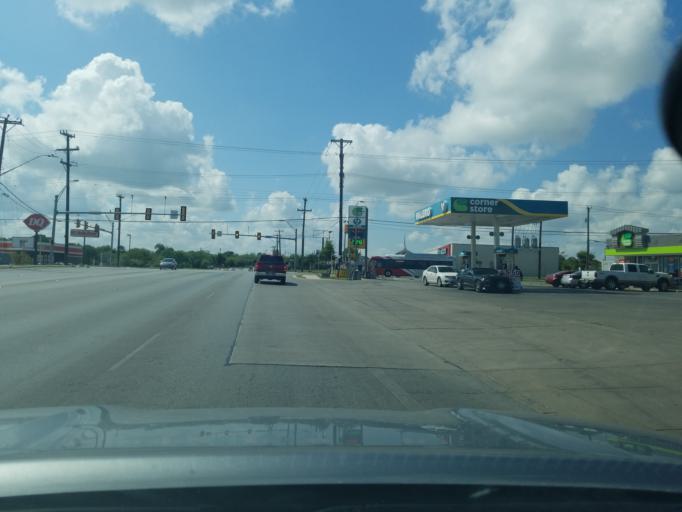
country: US
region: Texas
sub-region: Bexar County
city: Lackland Air Force Base
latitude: 29.3309
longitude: -98.5334
